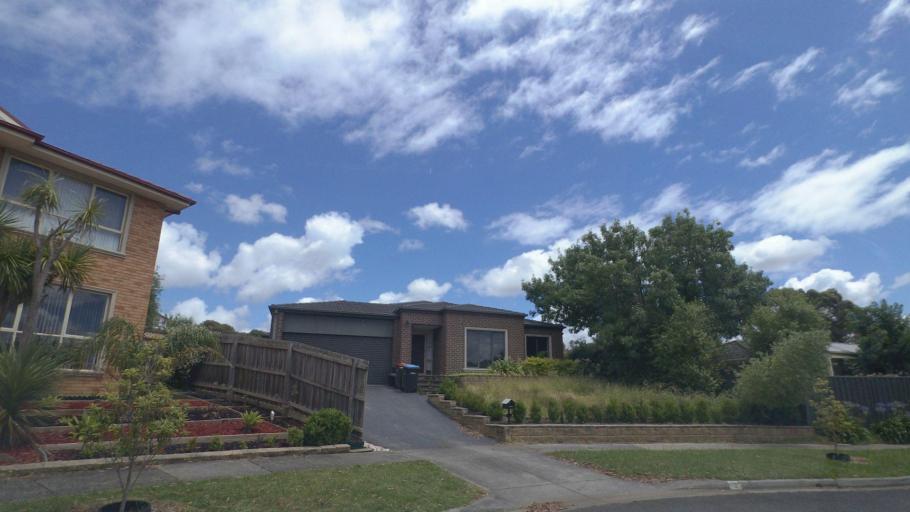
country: AU
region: Victoria
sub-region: Knox
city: Scoresby
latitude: -37.9069
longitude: 145.2490
